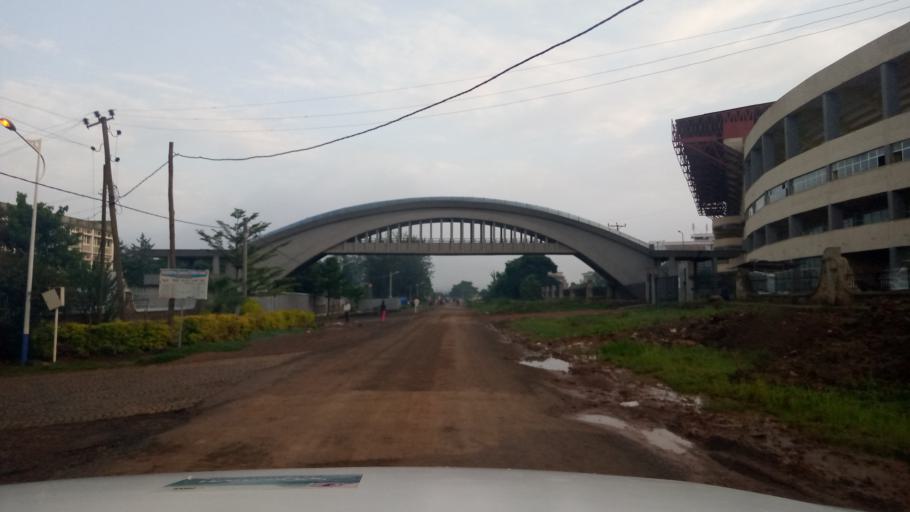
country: ET
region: Oromiya
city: Jima
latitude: 7.6760
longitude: 36.8525
